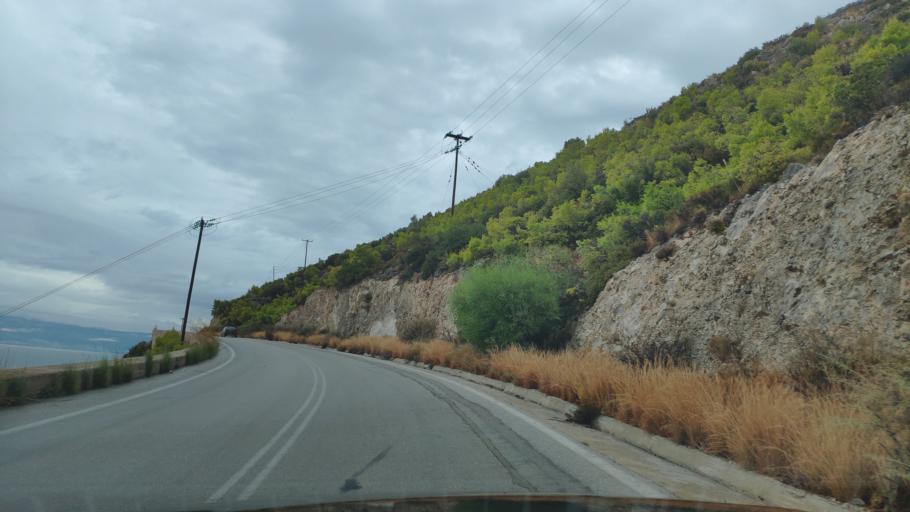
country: GR
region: Peloponnese
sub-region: Nomos Korinthias
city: Loutraki
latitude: 37.9833
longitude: 22.9741
